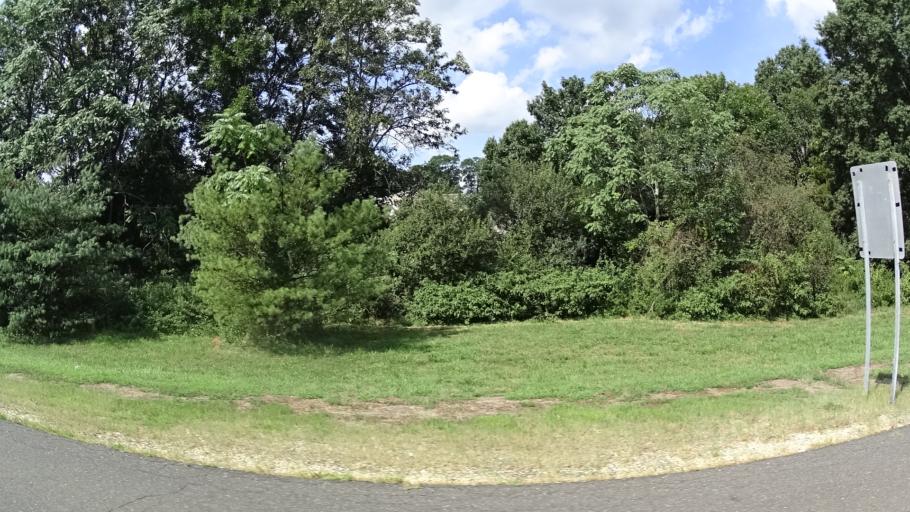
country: US
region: New Jersey
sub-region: Monmouth County
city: Tinton Falls
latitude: 40.3079
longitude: -74.0951
